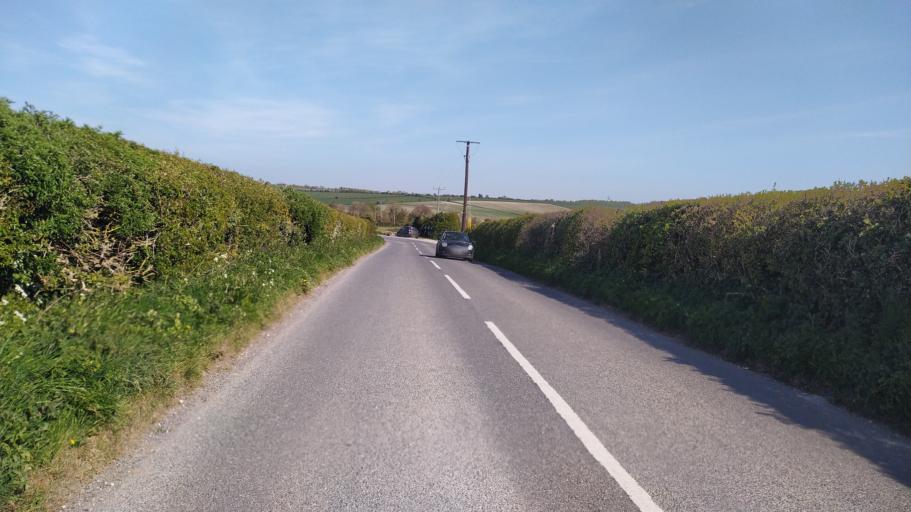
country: GB
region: England
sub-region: Dorset
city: Blandford Forum
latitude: 50.8843
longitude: -2.1445
